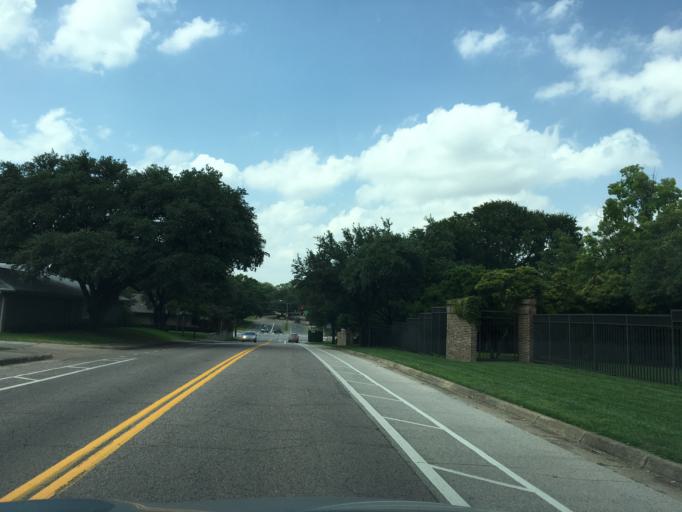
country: US
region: Texas
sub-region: Dallas County
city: University Park
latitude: 32.8788
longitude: -96.7787
